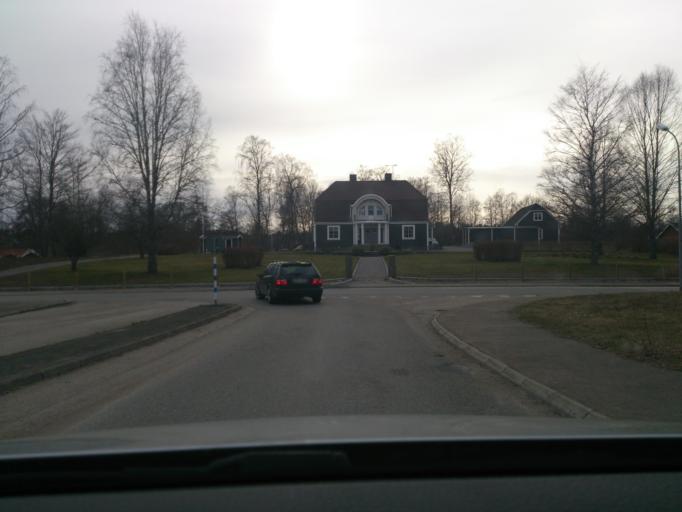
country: SE
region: Kronoberg
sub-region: Alvesta Kommun
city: Moheda
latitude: 57.0058
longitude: 14.5701
